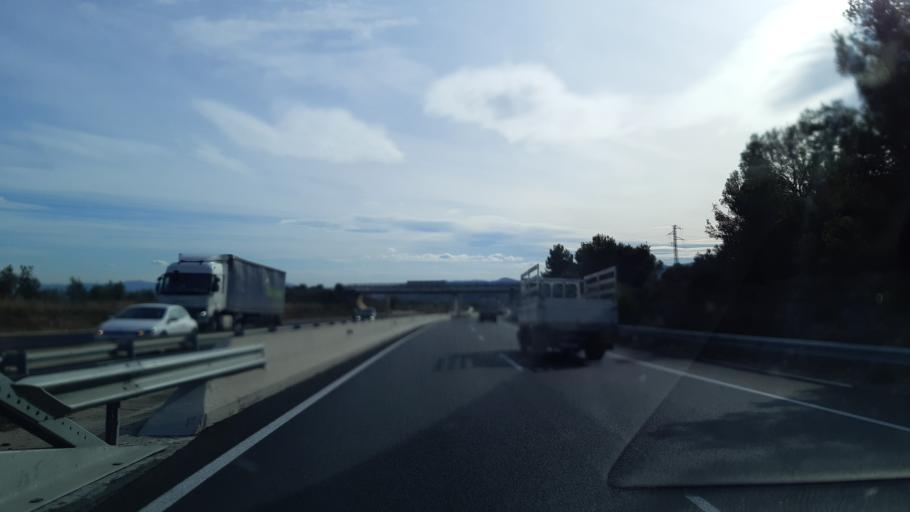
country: ES
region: Catalonia
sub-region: Provincia de Barcelona
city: Esparreguera
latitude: 41.5455
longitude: 1.8534
